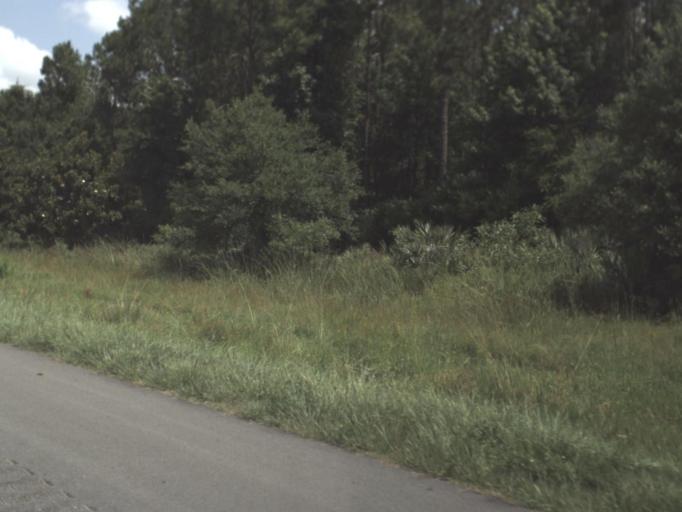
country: US
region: Georgia
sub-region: Echols County
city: Statenville
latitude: 30.6240
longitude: -83.1688
